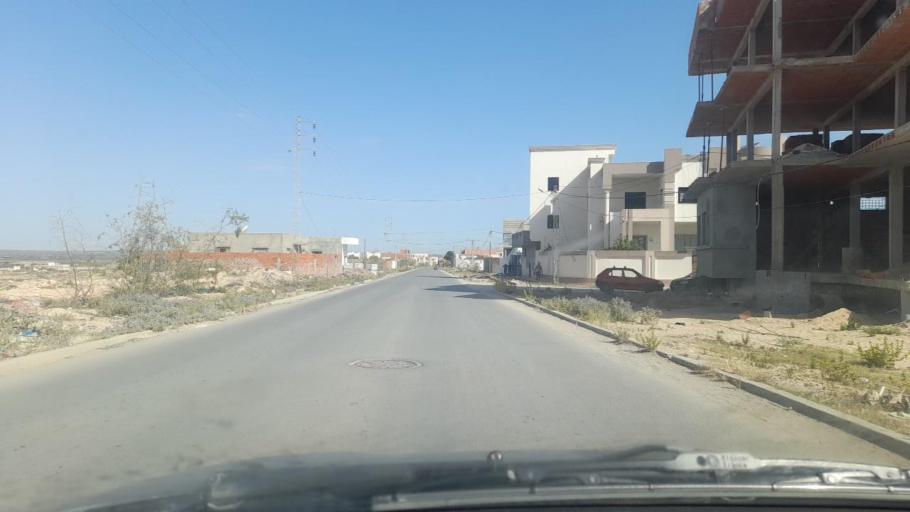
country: TN
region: Susah
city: Akouda
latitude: 35.8138
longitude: 10.5588
